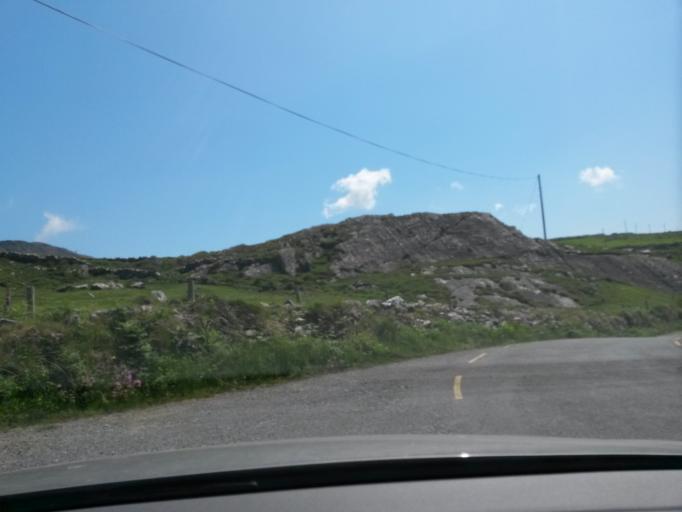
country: IE
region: Munster
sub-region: Ciarrai
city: Cahersiveen
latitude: 51.6518
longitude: -10.0561
